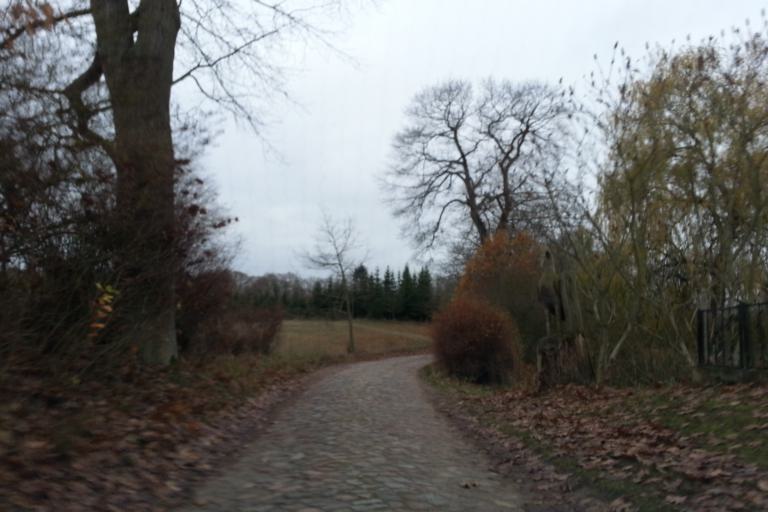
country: DE
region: Mecklenburg-Vorpommern
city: Ferdinandshof
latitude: 53.5887
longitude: 13.8393
